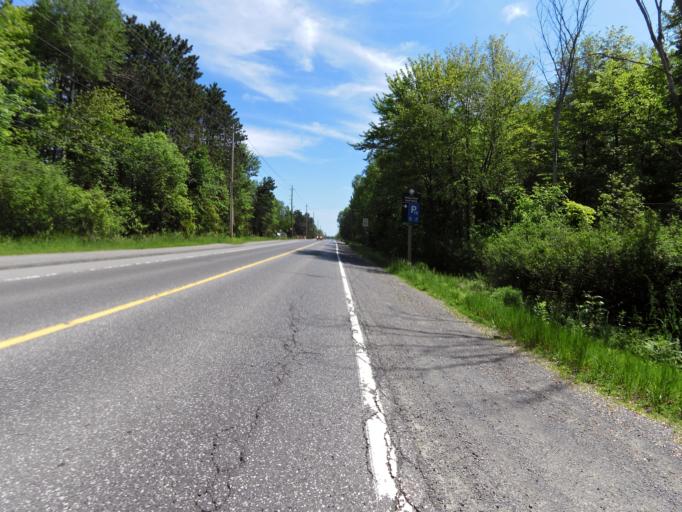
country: CA
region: Ontario
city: Ottawa
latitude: 45.3221
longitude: -75.7289
